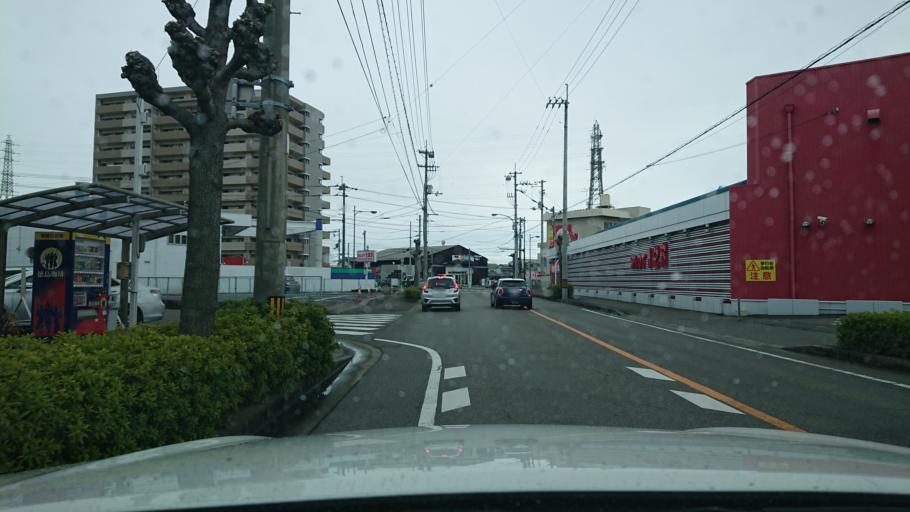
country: JP
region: Tokushima
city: Tokushima-shi
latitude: 34.0859
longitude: 134.5390
